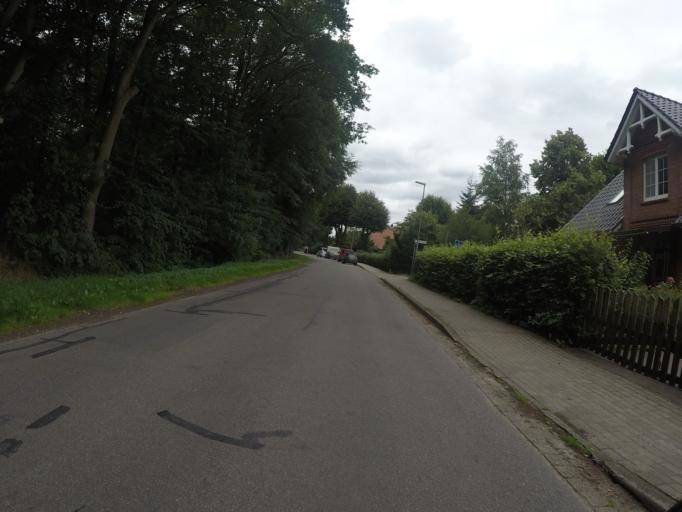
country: DE
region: Lower Saxony
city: Himmelpforten
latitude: 53.6147
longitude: 9.3172
